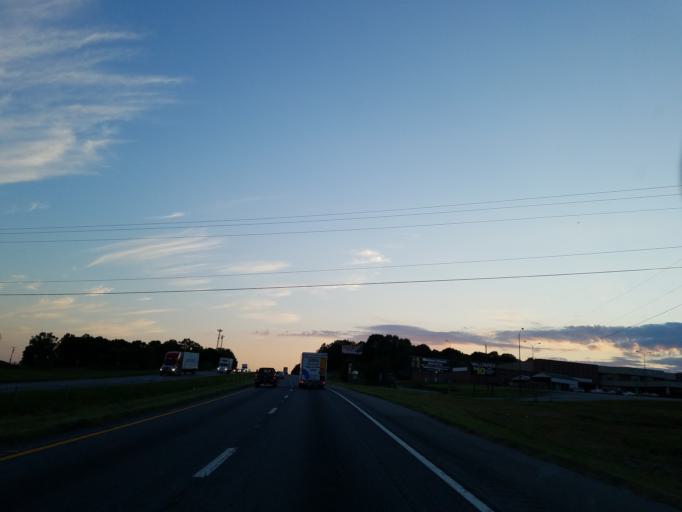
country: US
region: South Carolina
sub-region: Spartanburg County
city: Cowpens
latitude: 35.0717
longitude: -81.7607
